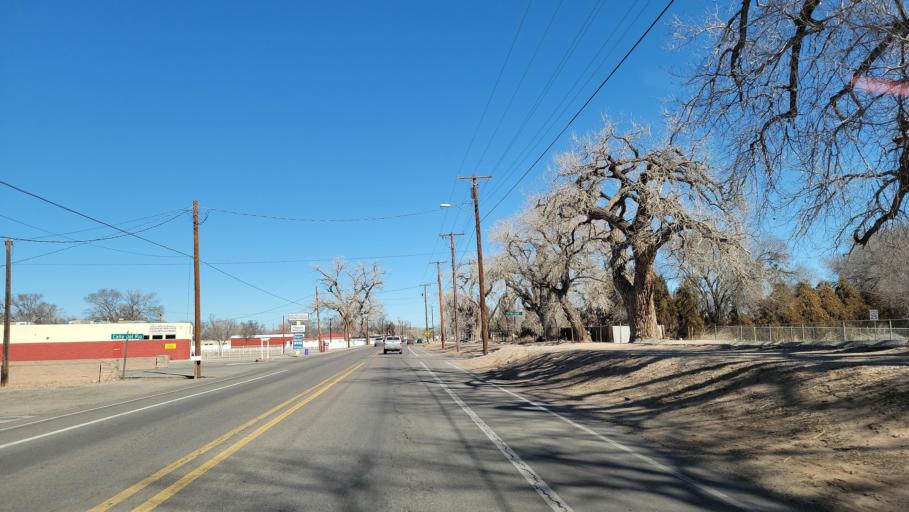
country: US
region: New Mexico
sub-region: Bernalillo County
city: South Valley
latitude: 35.0092
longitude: -106.6881
